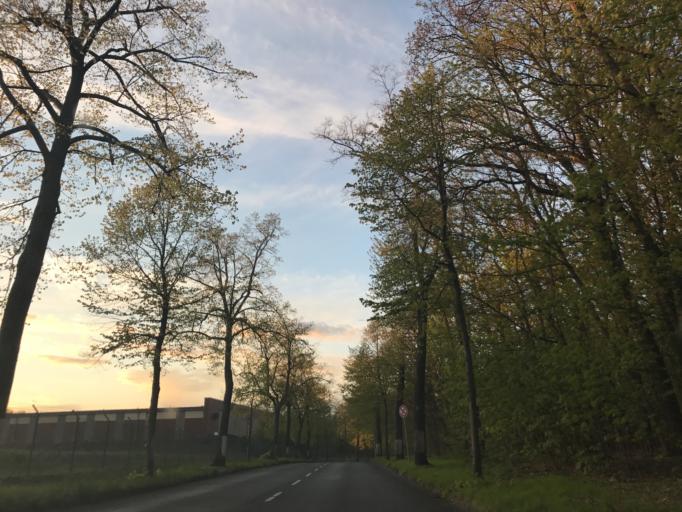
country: DE
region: Berlin
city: Haselhorst
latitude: 52.5156
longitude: 13.2189
